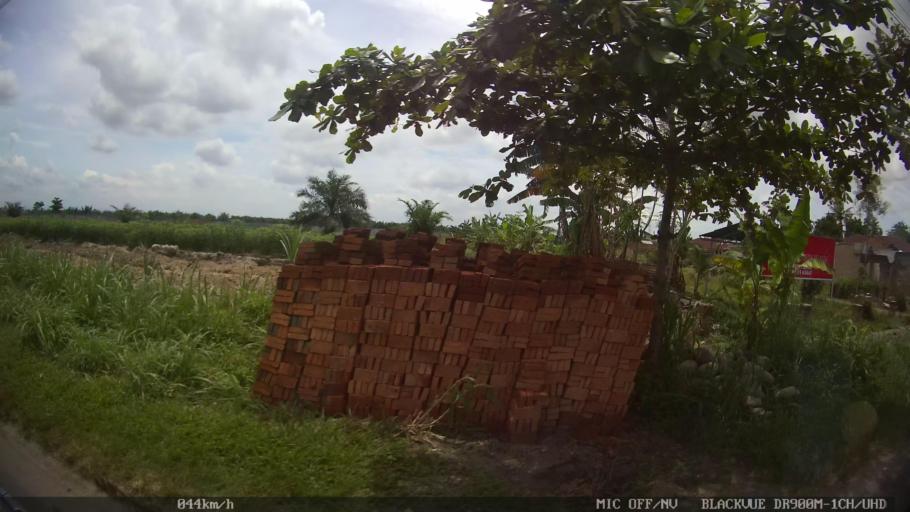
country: ID
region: North Sumatra
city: Percut
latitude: 3.5830
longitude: 98.8832
